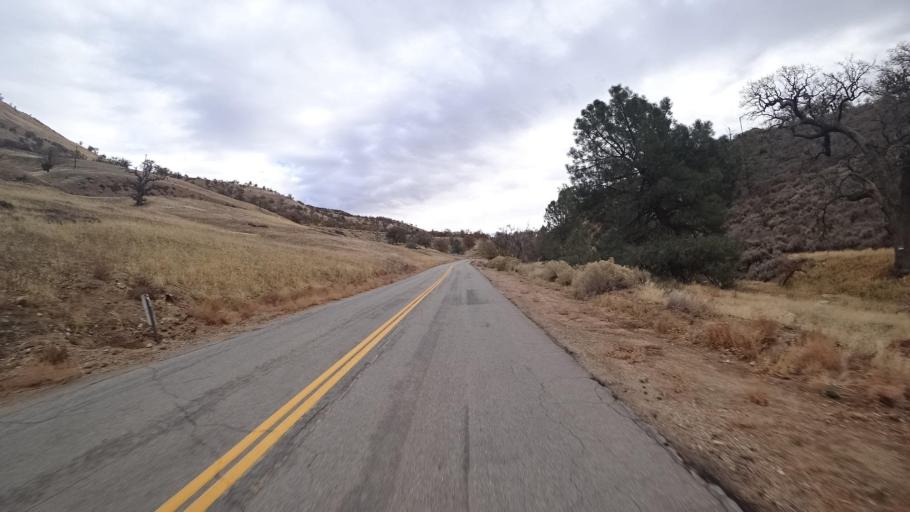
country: US
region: California
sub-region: Kern County
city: Golden Hills
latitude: 35.1341
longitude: -118.5599
